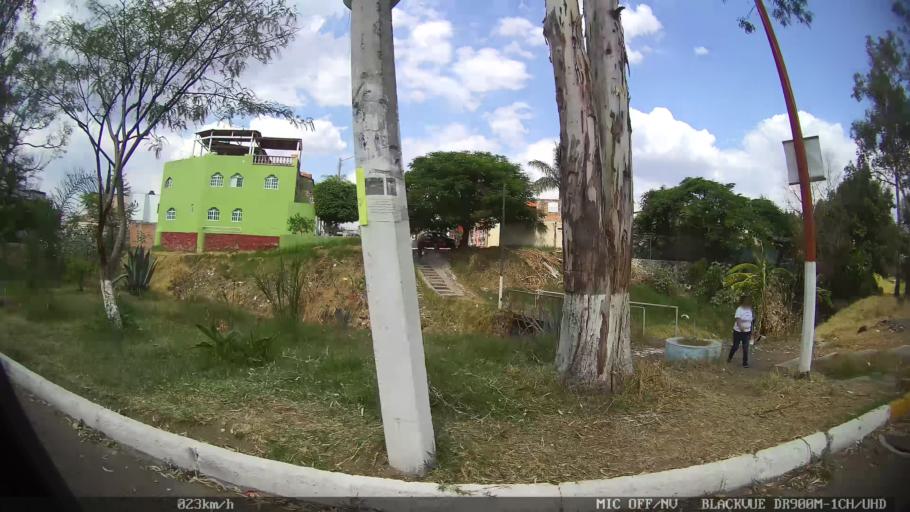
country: MX
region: Jalisco
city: Tlaquepaque
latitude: 20.6259
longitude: -103.2660
